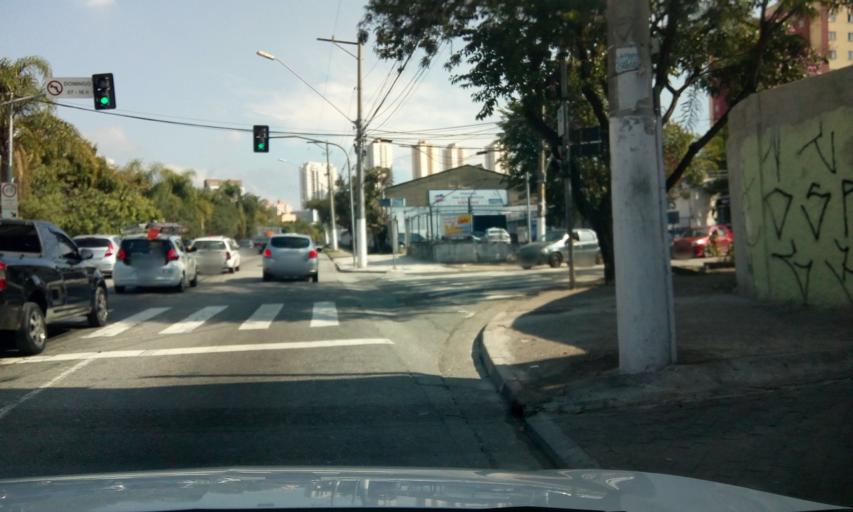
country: BR
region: Sao Paulo
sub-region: Osasco
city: Osasco
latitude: -23.5521
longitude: -46.7780
